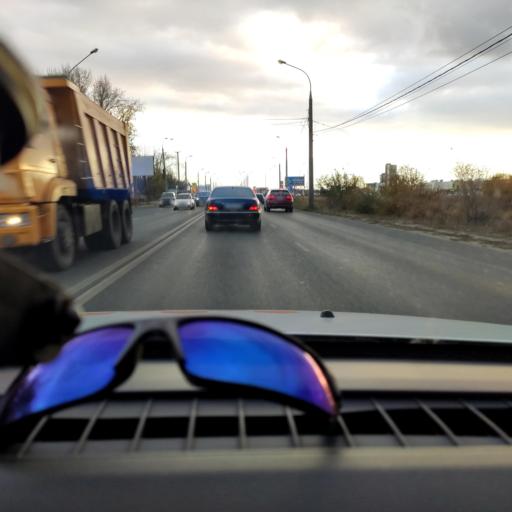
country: RU
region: Samara
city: Samara
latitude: 53.1447
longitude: 50.1820
